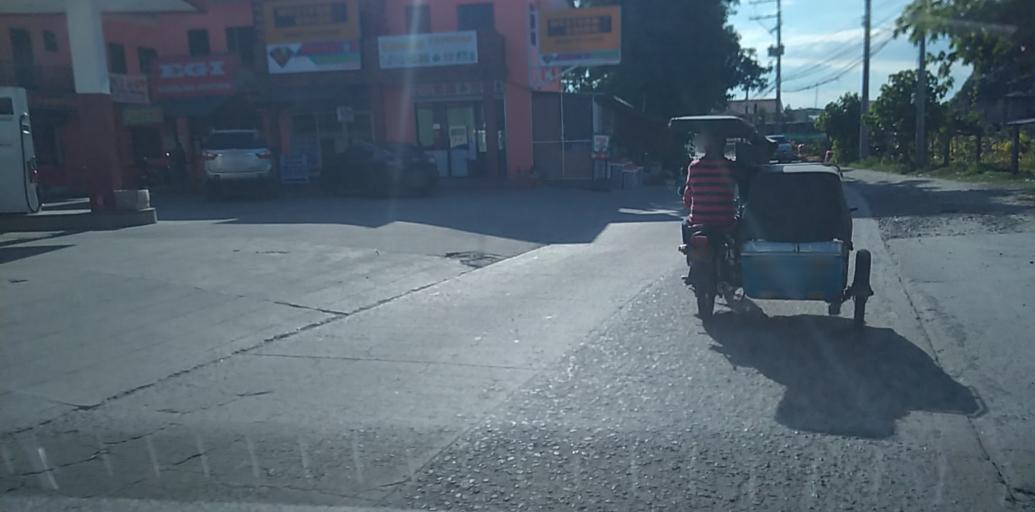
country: PH
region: Central Luzon
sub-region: Province of Pampanga
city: Acli
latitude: 15.1125
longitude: 120.6328
